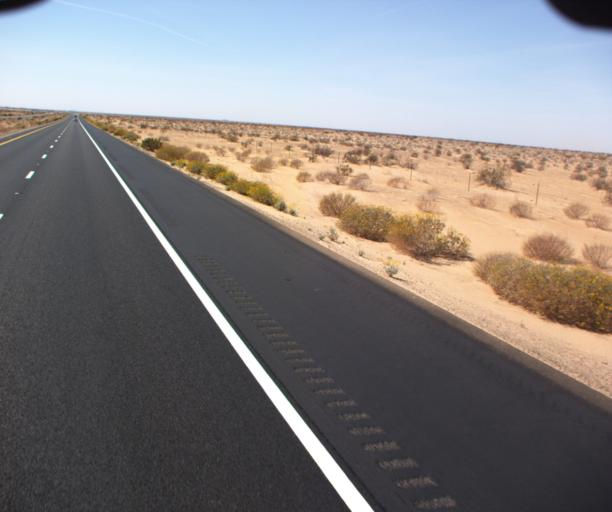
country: US
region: Arizona
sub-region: Yuma County
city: Somerton
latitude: 32.4954
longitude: -114.5984
